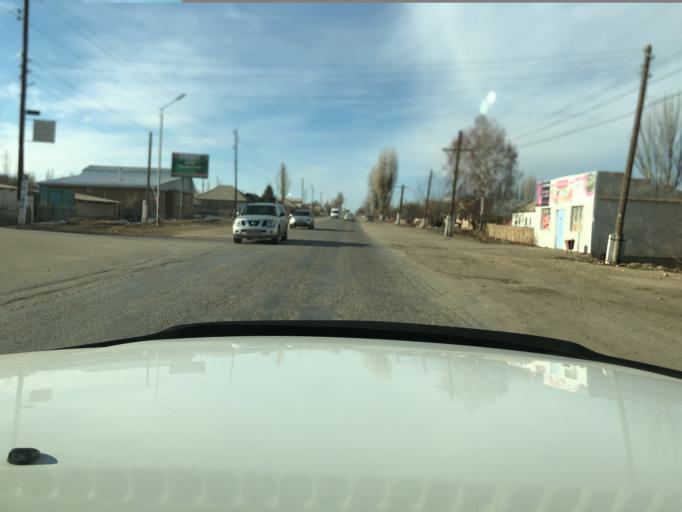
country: KG
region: Ysyk-Koel
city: Pokrovka
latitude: 42.3237
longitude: 77.9319
